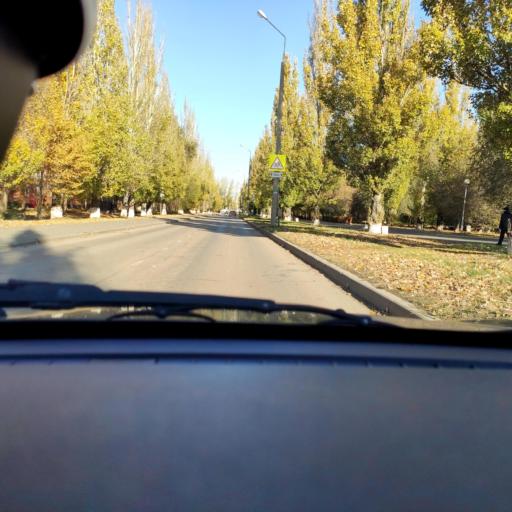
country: RU
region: Samara
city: Tol'yatti
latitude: 53.5355
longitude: 49.2729
